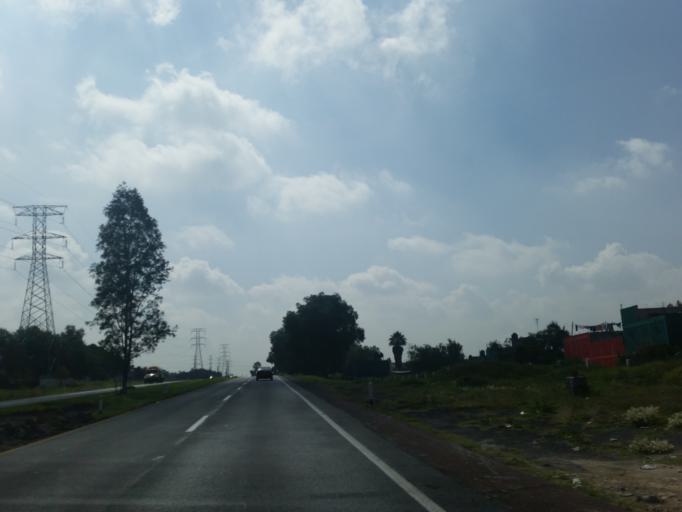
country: MX
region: Mexico
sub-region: Acolman de Nezahualcoyotl
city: Prados de San Juan
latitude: 19.6223
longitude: -98.9885
